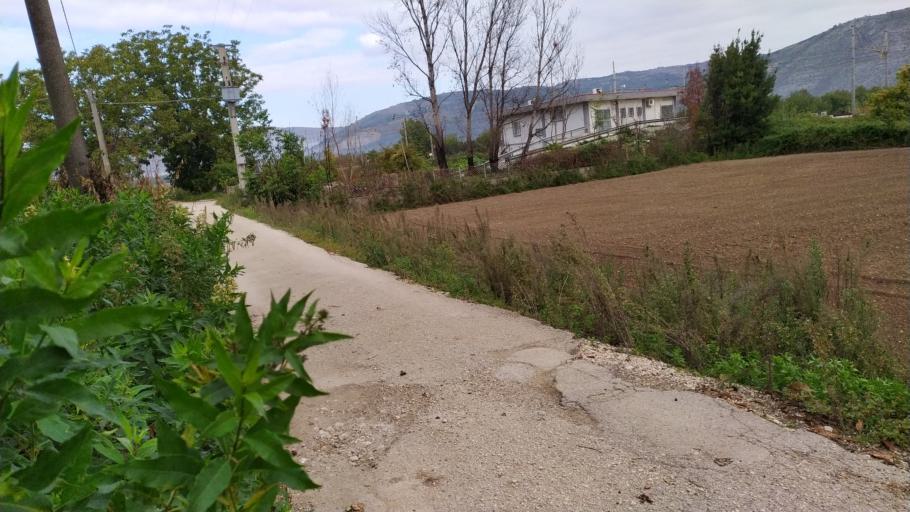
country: IT
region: Campania
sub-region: Provincia di Caserta
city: Montedecoro
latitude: 41.0174
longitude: 14.4055
